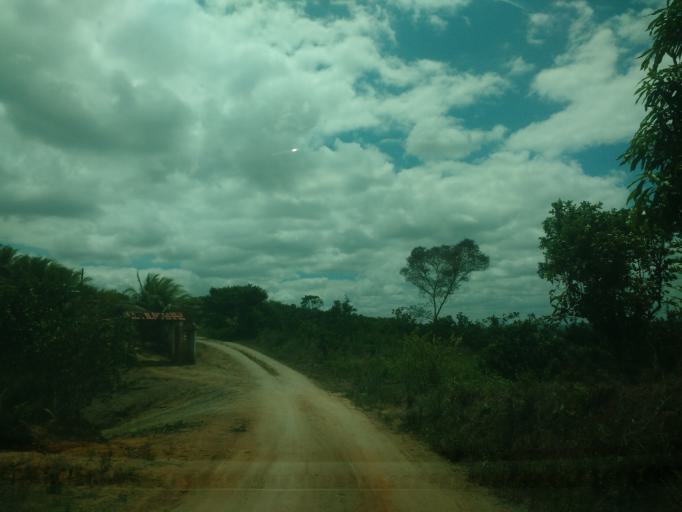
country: BR
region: Alagoas
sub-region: Santana Do Mundau
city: Santana do Mundau
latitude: -9.1579
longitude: -36.1600
